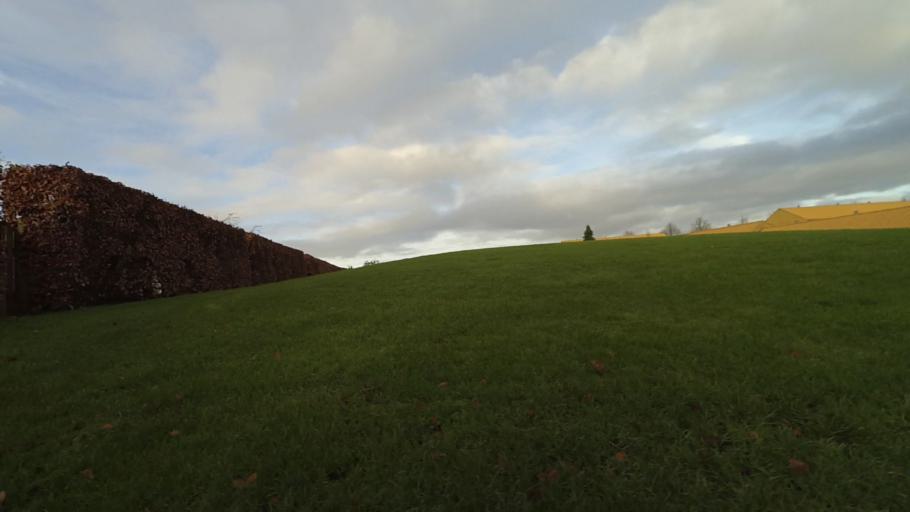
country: DK
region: Central Jutland
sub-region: Arhus Kommune
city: Marslet
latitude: 56.1046
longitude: 10.1705
